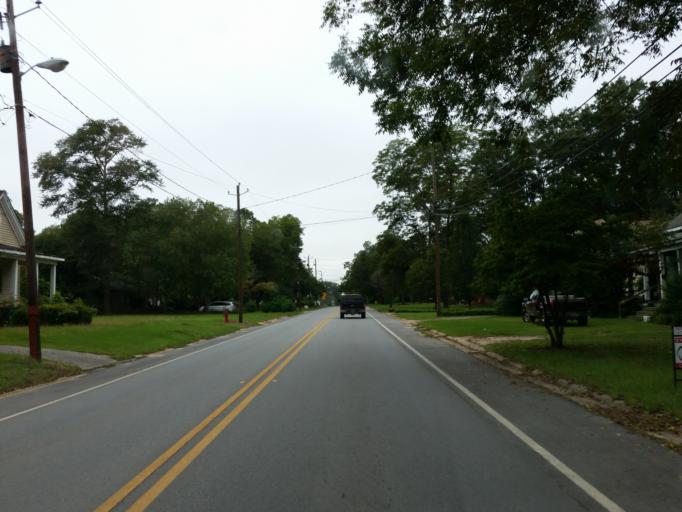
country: US
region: Georgia
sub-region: Dooly County
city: Unadilla
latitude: 32.2605
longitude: -83.7391
